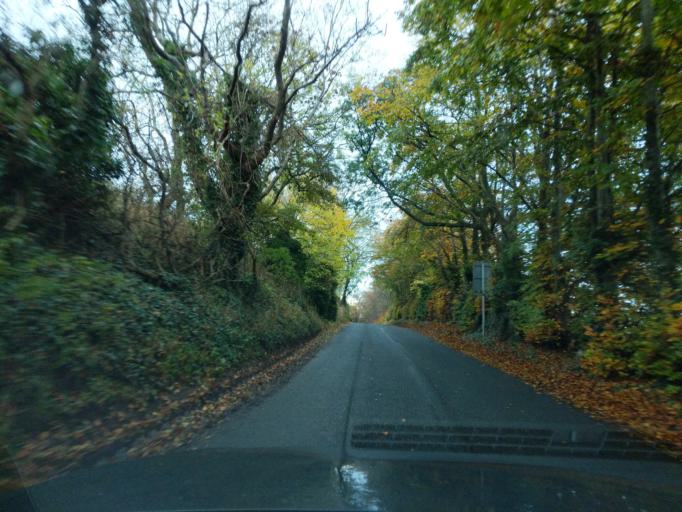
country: GB
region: Scotland
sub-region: East Lothian
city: Dunbar
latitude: 55.9763
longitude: -2.5196
